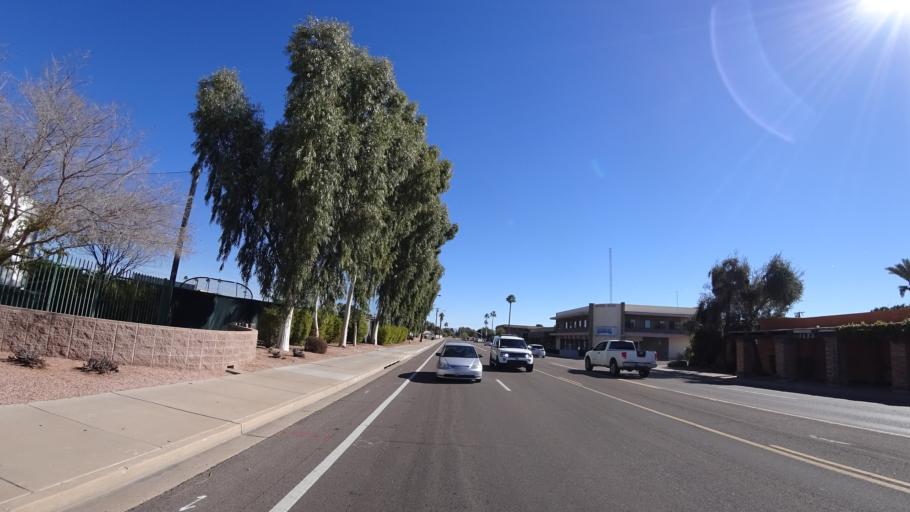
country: US
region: Arizona
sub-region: Maricopa County
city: Scottsdale
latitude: 33.4877
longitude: -111.9201
